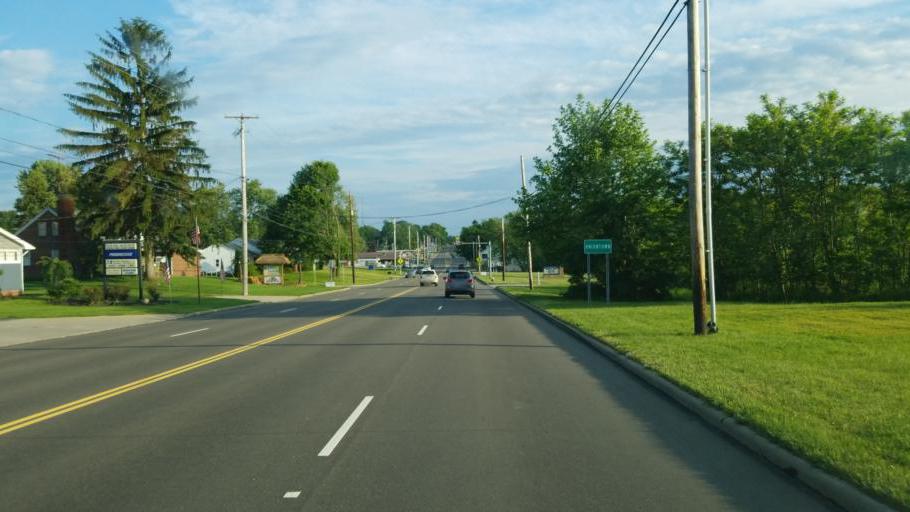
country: US
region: Ohio
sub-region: Stark County
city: Uniontown
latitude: 40.9805
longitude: -81.4068
